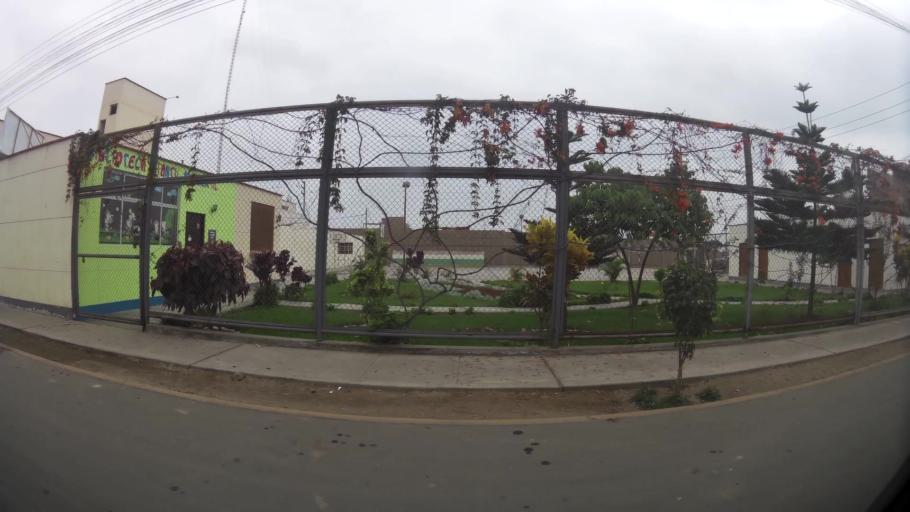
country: PE
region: Lima
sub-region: Provincia de Huaral
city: Huaral
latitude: -11.4900
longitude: -77.1996
